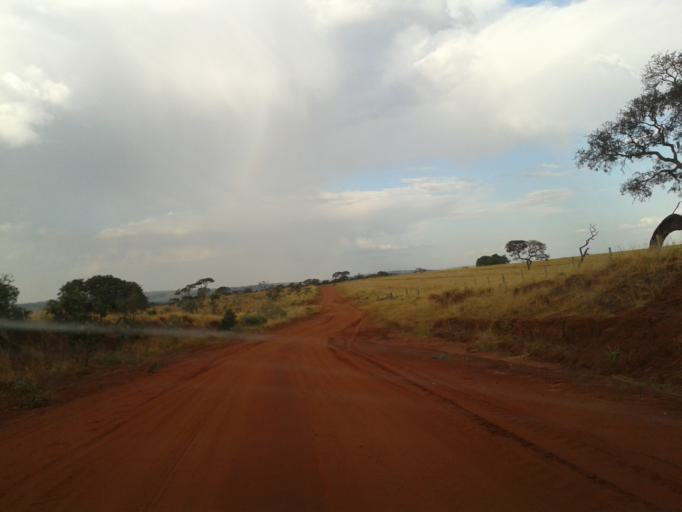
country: BR
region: Minas Gerais
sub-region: Santa Vitoria
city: Santa Vitoria
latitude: -19.1901
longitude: -49.8717
